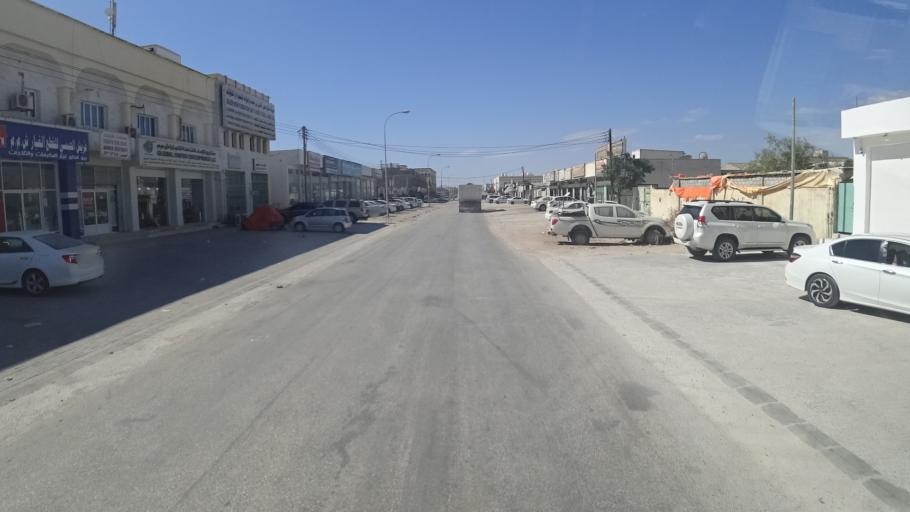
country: OM
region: Zufar
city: Salalah
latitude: 17.0169
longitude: 54.0521
